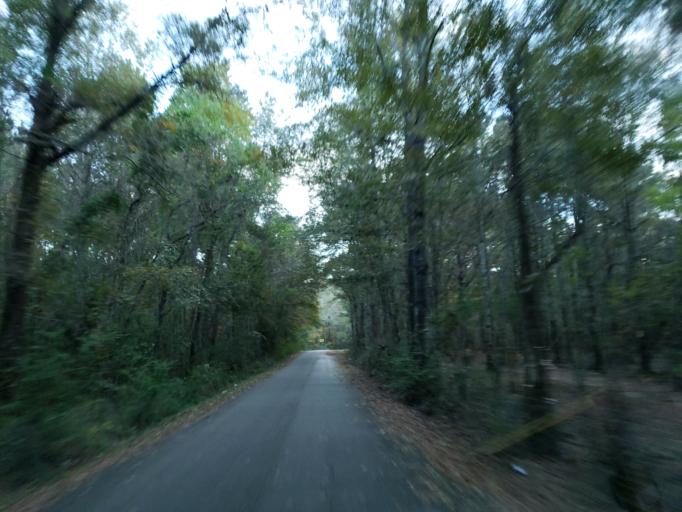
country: US
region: Mississippi
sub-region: Forrest County
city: Hattiesburg
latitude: 31.2823
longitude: -89.2543
